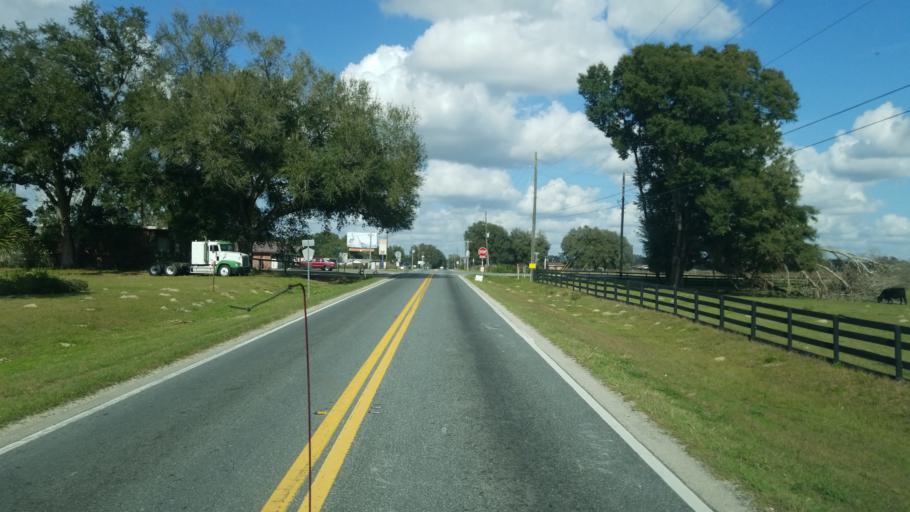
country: US
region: Florida
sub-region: Marion County
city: Belleview
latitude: 28.9810
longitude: -82.1199
